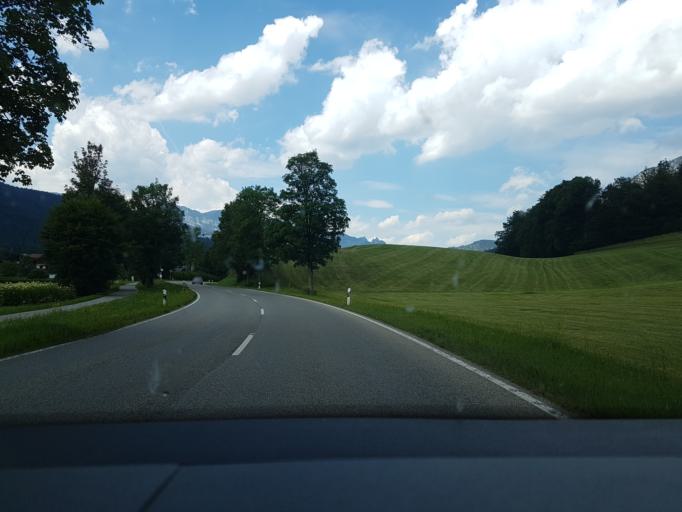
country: DE
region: Bavaria
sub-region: Upper Bavaria
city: Berchtesgaden
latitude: 47.6359
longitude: 12.9758
